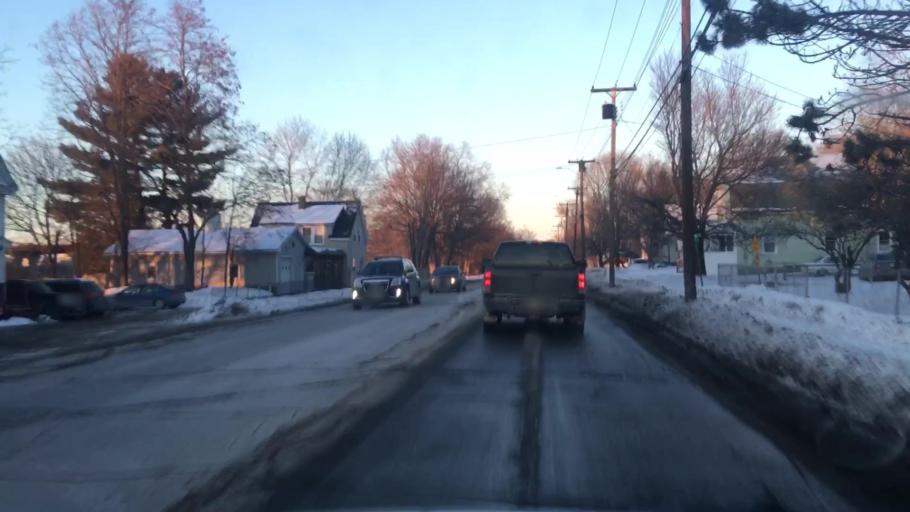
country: US
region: Maine
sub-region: Penobscot County
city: Bangor
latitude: 44.7787
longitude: -68.7767
